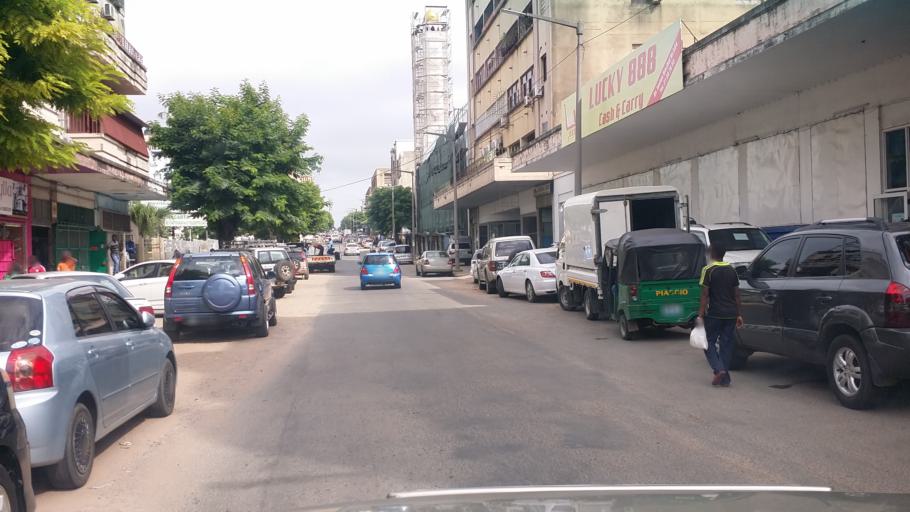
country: MZ
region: Maputo City
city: Maputo
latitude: -25.9664
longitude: 32.5687
